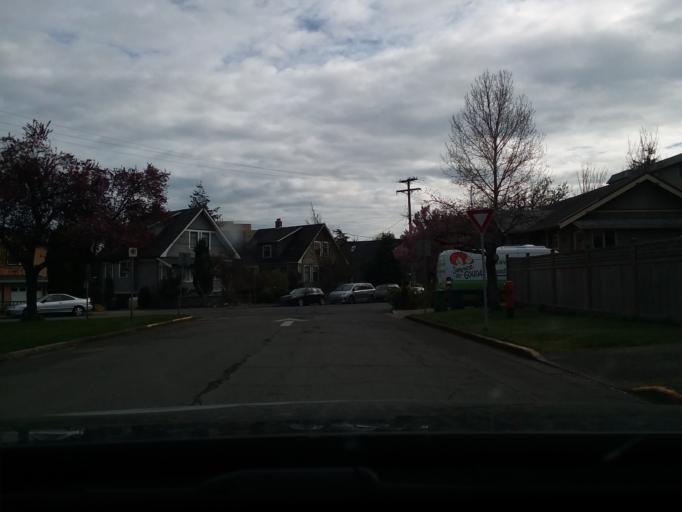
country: CA
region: British Columbia
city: Oak Bay
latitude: 48.4308
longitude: -123.3324
